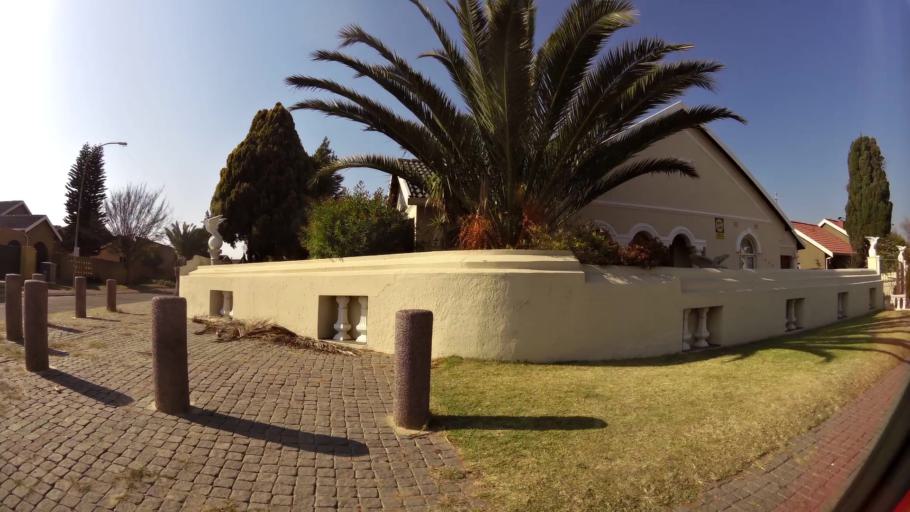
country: ZA
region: Gauteng
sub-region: City of Johannesburg Metropolitan Municipality
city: Soweto
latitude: -26.2485
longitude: 27.9550
